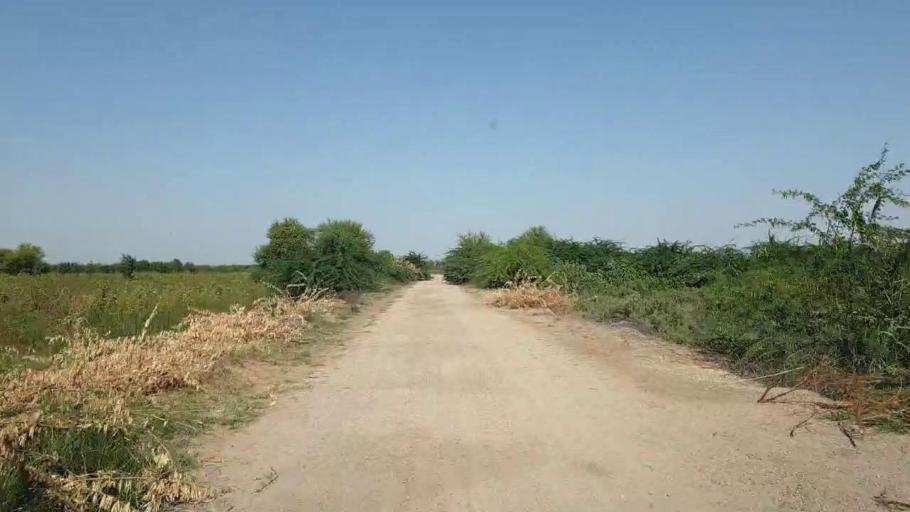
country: PK
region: Sindh
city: Tando Bago
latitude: 24.7342
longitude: 69.0428
